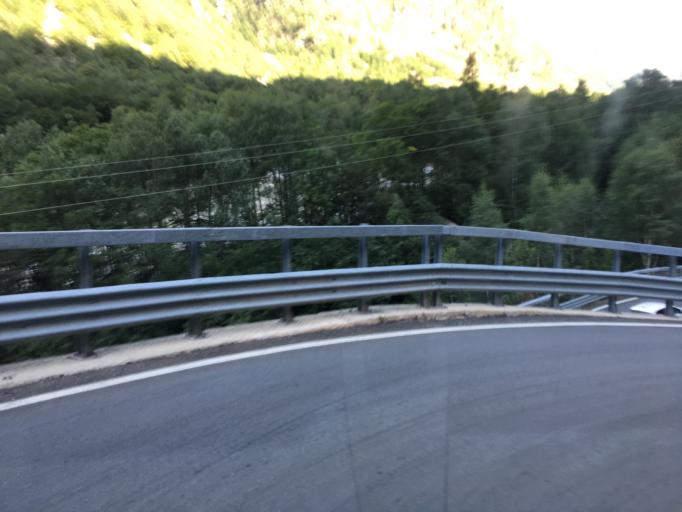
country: IT
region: Lombardy
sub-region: Provincia di Sondrio
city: San Giacomo Filippo
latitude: 46.3610
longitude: 9.3642
